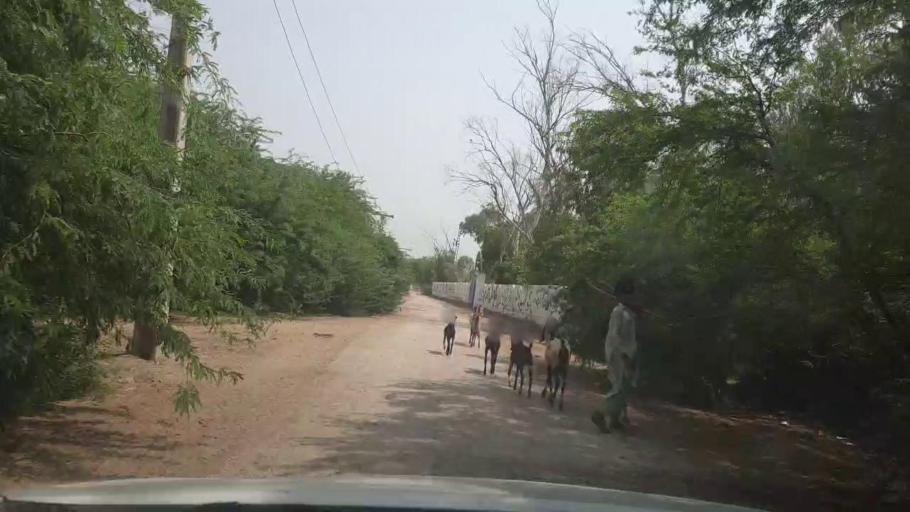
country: PK
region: Sindh
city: Kot Diji
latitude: 27.3433
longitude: 68.7154
